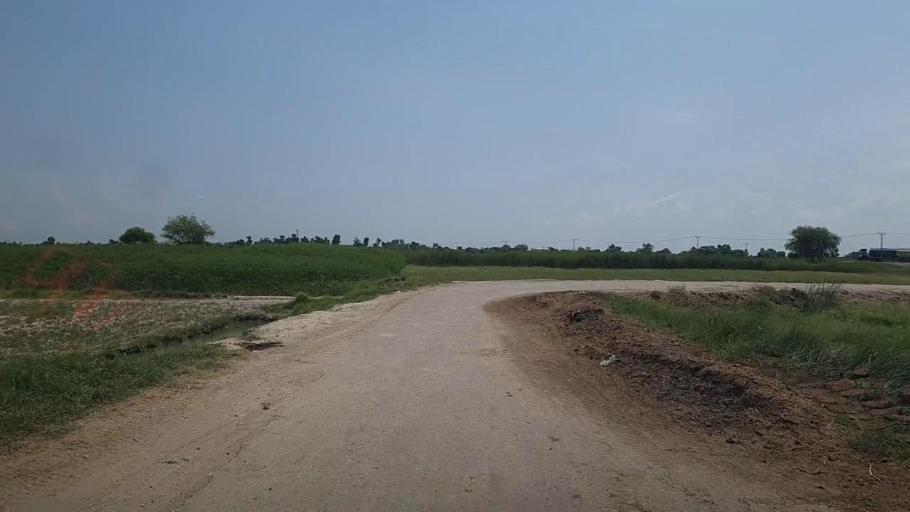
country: PK
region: Sindh
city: Ubauro
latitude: 28.1846
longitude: 69.8004
